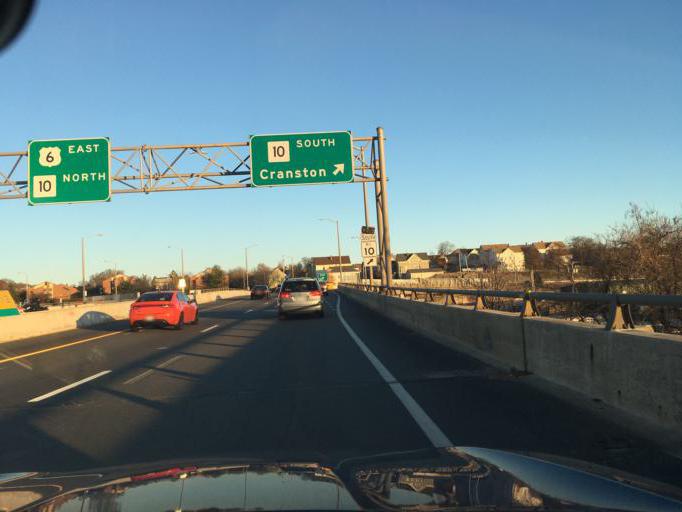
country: US
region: Rhode Island
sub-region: Providence County
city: Providence
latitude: 41.8139
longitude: -71.4421
